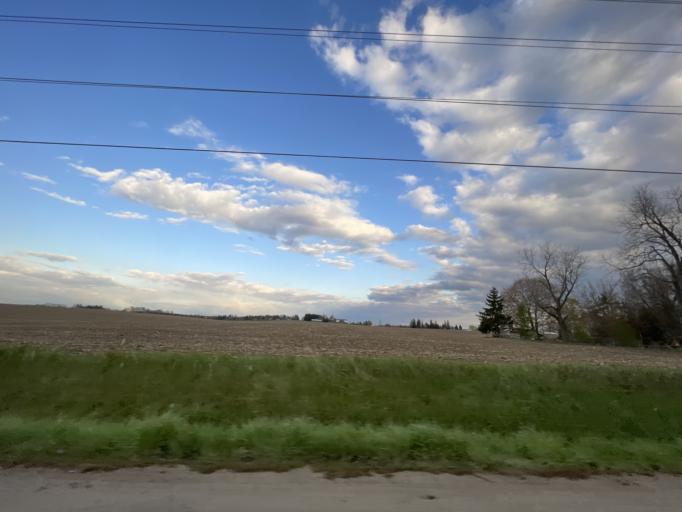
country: CA
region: Ontario
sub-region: Wellington County
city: Guelph
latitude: 43.5872
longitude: -80.2975
